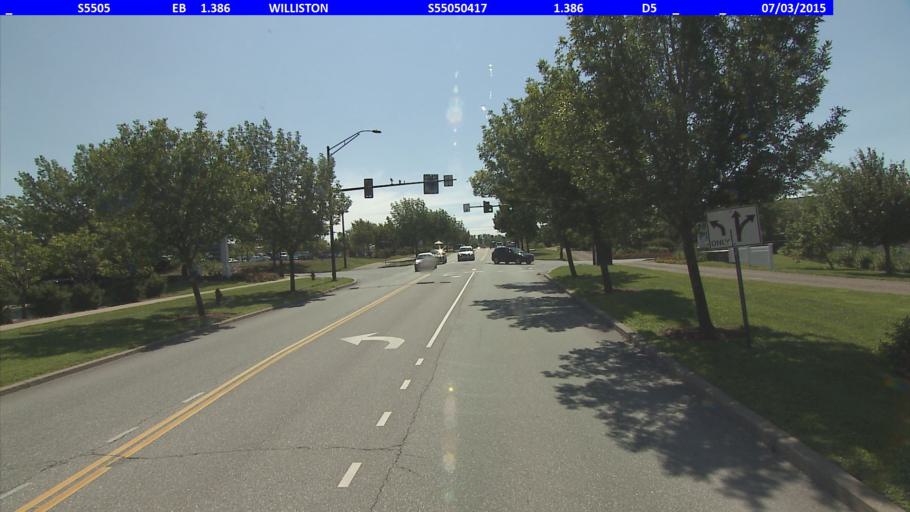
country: US
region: Vermont
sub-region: Chittenden County
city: Essex Junction
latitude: 44.4452
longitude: -73.1159
